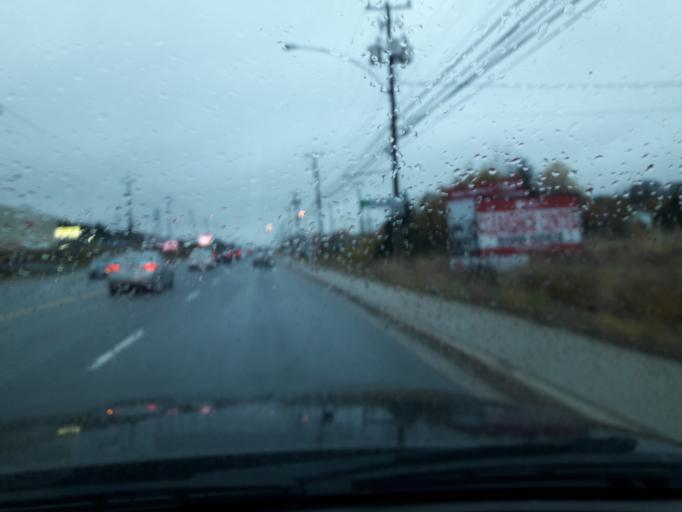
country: CA
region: Newfoundland and Labrador
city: Mount Pearl
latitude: 47.5499
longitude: -52.7797
